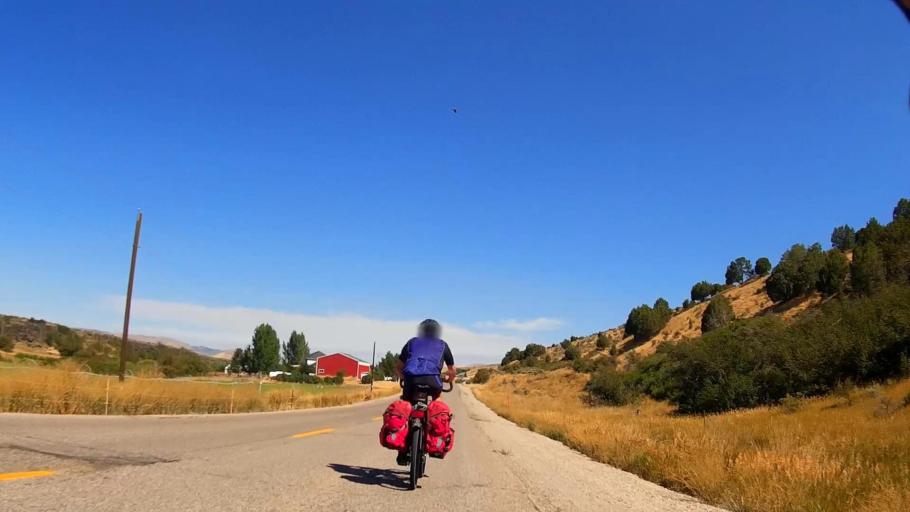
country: US
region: Idaho
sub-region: Bannock County
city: Pocatello
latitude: 42.7147
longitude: -112.2075
